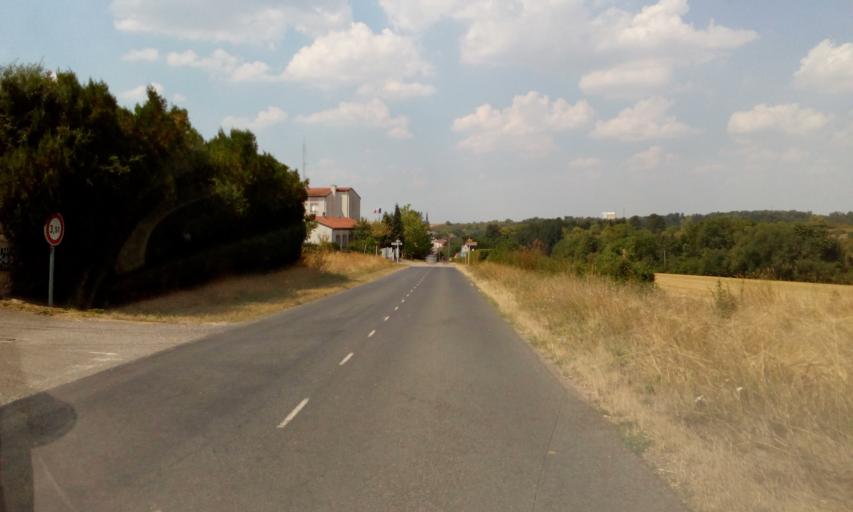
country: FR
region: Lorraine
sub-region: Departement de Meurthe-et-Moselle
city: Pagny-sur-Moselle
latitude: 48.9486
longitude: 5.8735
